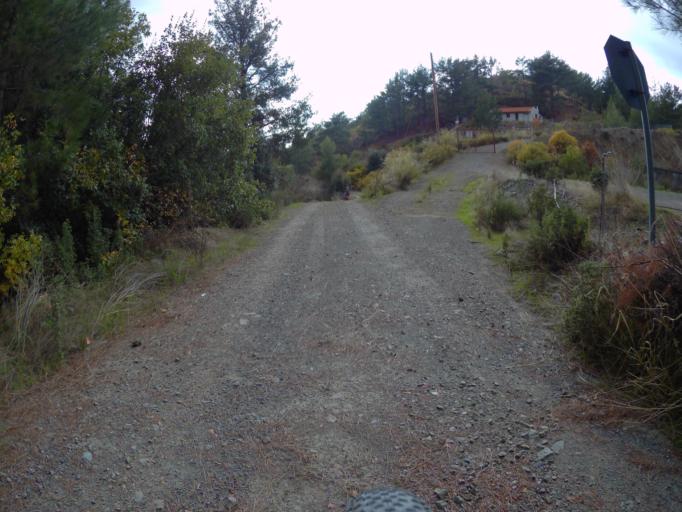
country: CY
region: Lefkosia
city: Kakopetria
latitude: 34.9175
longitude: 32.8138
